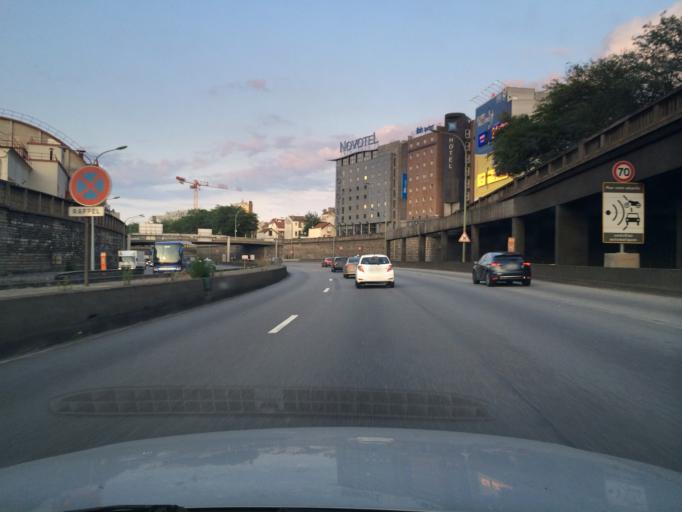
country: FR
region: Ile-de-France
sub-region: Departement du Val-de-Marne
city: Le Kremlin-Bicetre
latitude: 48.8160
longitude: 2.3620
